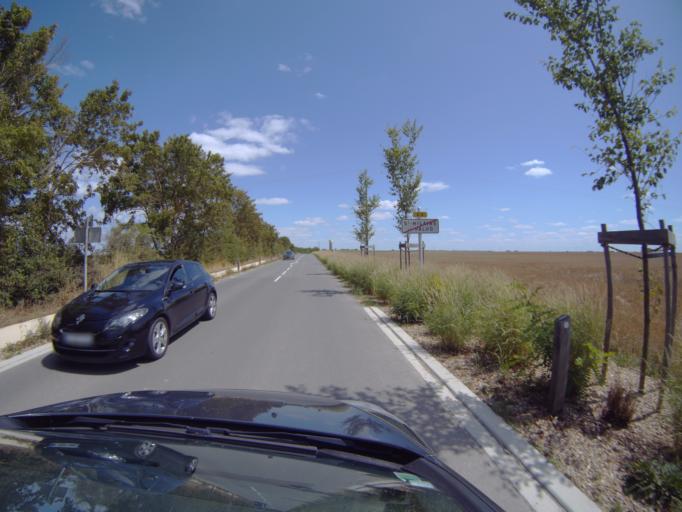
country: FR
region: Poitou-Charentes
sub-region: Departement des Deux-Sevres
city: Saint-Hilaire-la-Palud
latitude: 46.2601
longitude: -0.7070
